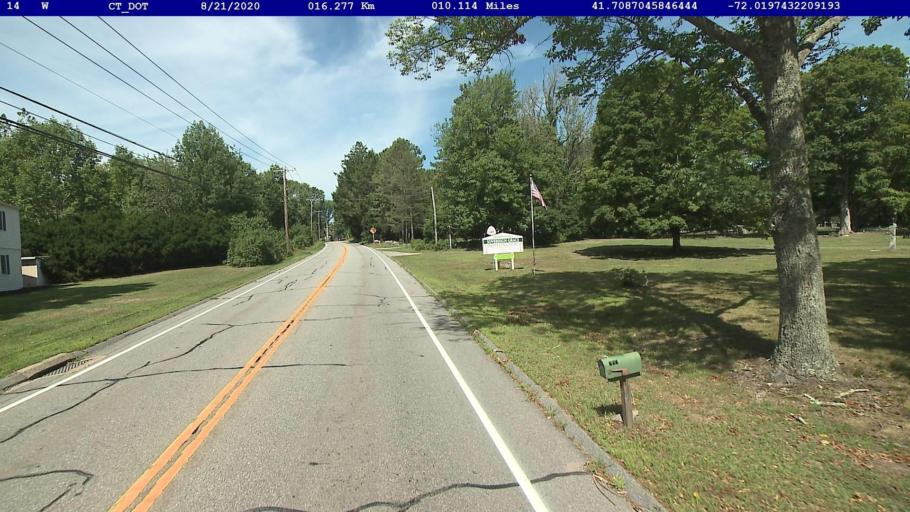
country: US
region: Connecticut
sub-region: Windham County
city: Plainfield Village
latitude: 41.7087
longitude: -72.0198
